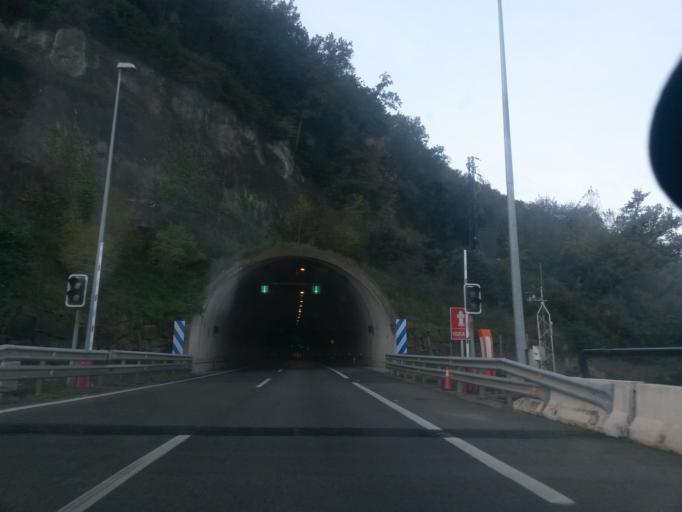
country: ES
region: Catalonia
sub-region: Provincia de Girona
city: Sant Joan les Fonts
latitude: 42.2173
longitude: 2.5640
